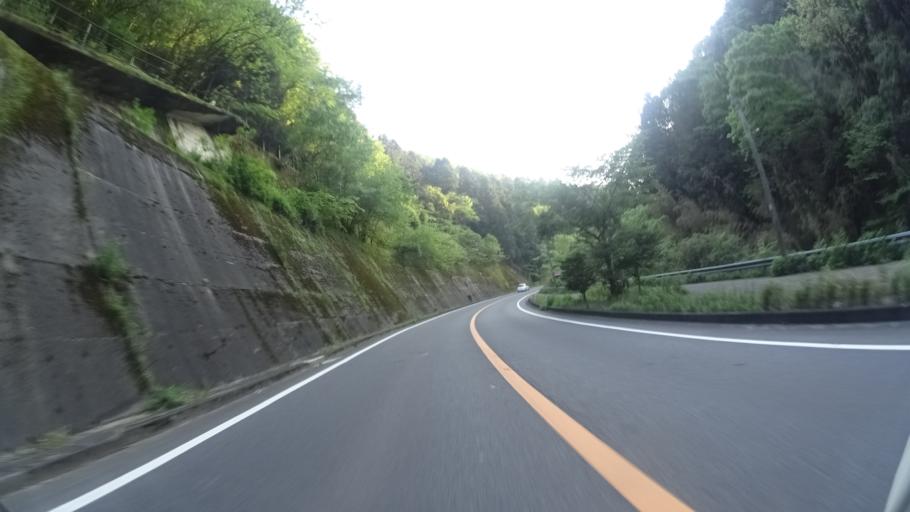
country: JP
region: Tokushima
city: Ikedacho
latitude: 34.0146
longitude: 133.7698
